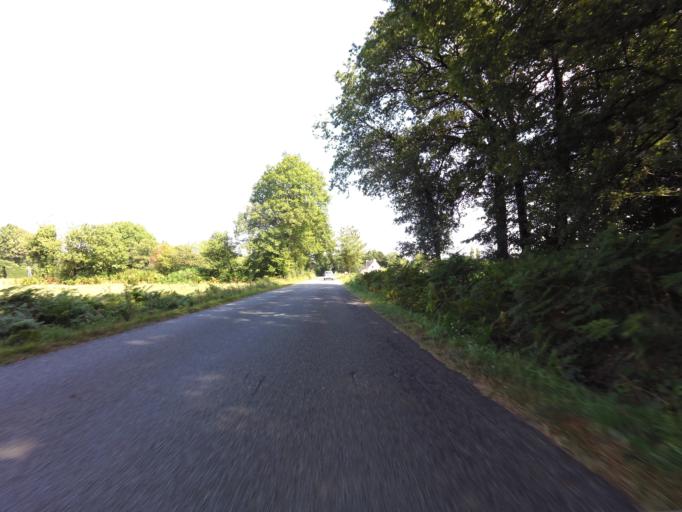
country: FR
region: Brittany
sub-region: Departement du Morbihan
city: Limerzel
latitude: 47.6437
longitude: -2.3665
